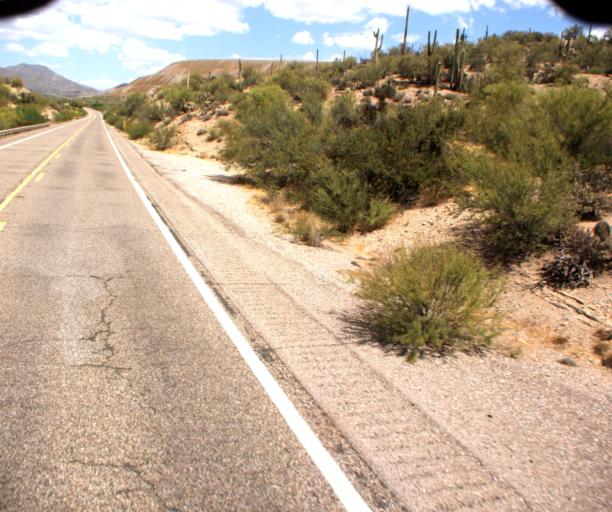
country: US
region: Arizona
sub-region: Pinal County
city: Kearny
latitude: 33.1107
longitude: -110.9536
